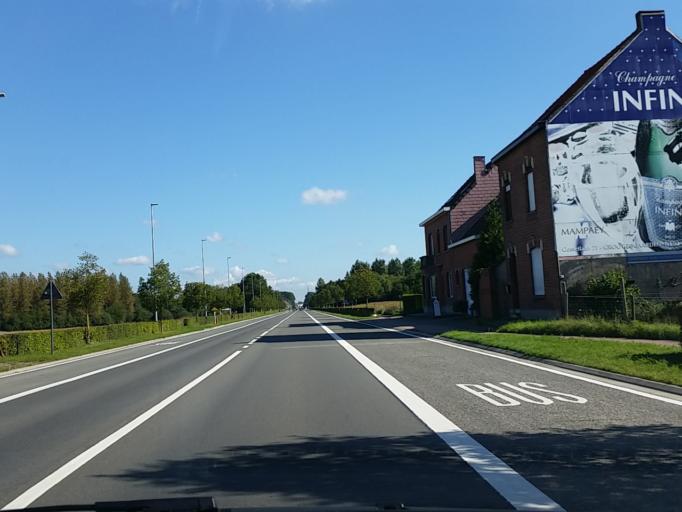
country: BE
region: Flanders
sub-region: Provincie Vlaams-Brabant
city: Kampenhout
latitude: 50.9462
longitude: 4.5717
